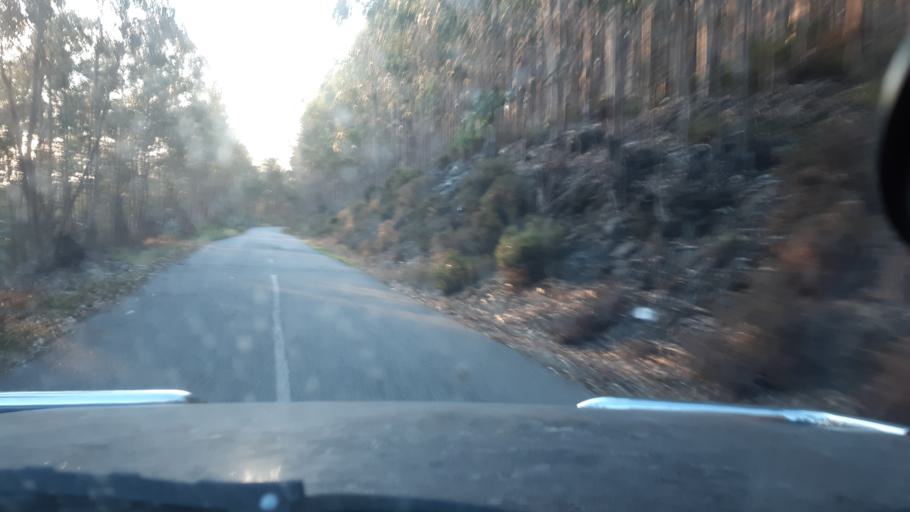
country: PT
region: Aveiro
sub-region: Agueda
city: Aguada de Cima
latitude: 40.5569
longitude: -8.2918
